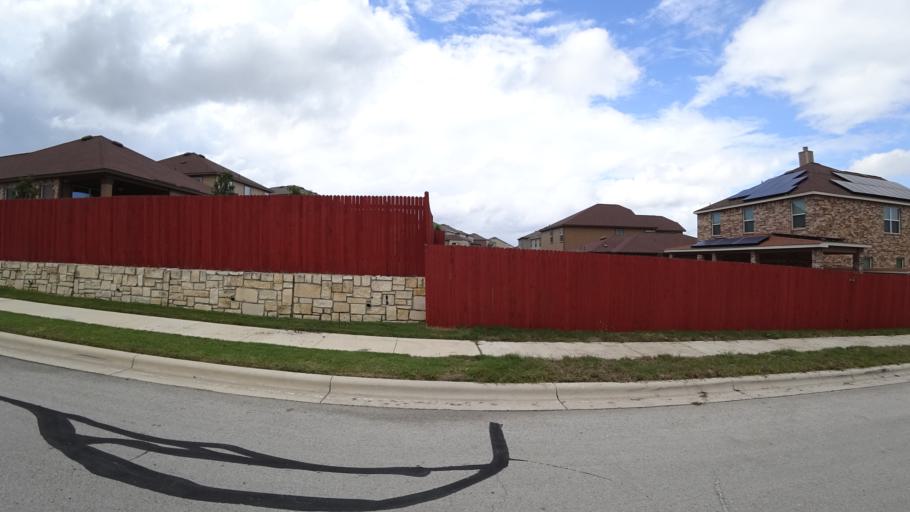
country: US
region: Texas
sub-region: Travis County
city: Onion Creek
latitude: 30.1476
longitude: -97.7422
